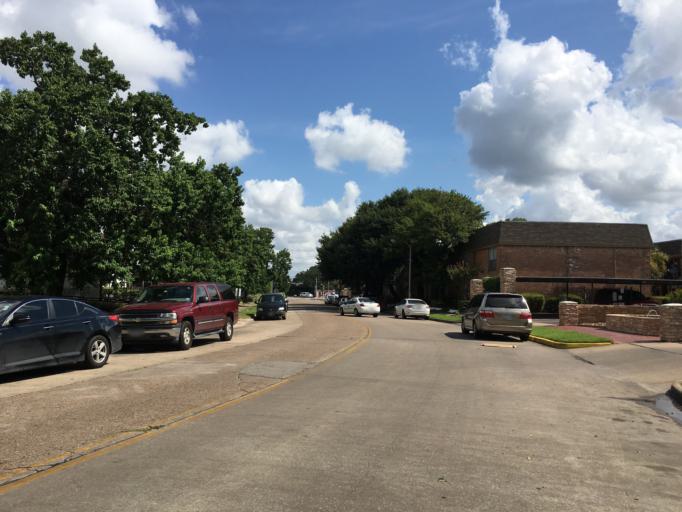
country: US
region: Texas
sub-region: Harris County
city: Piney Point Village
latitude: 29.7356
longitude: -95.5051
